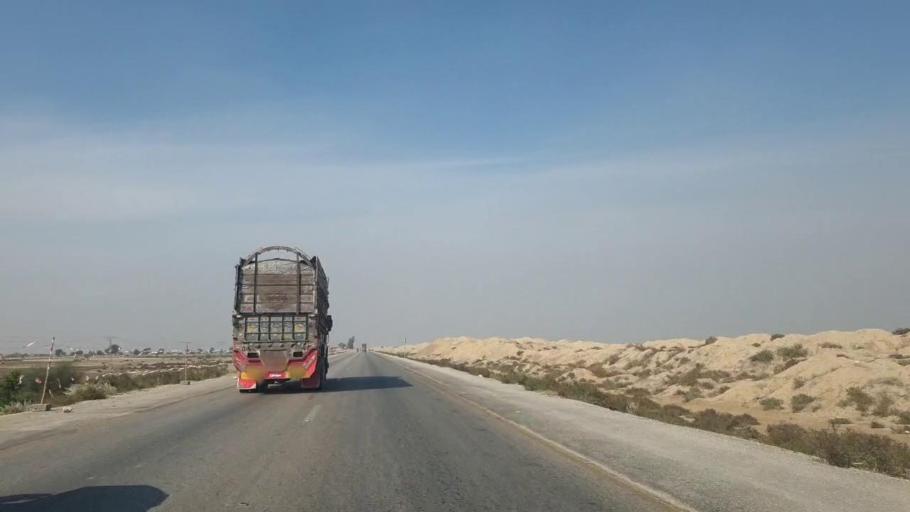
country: PK
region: Sindh
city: Sann
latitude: 25.9556
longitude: 68.1943
